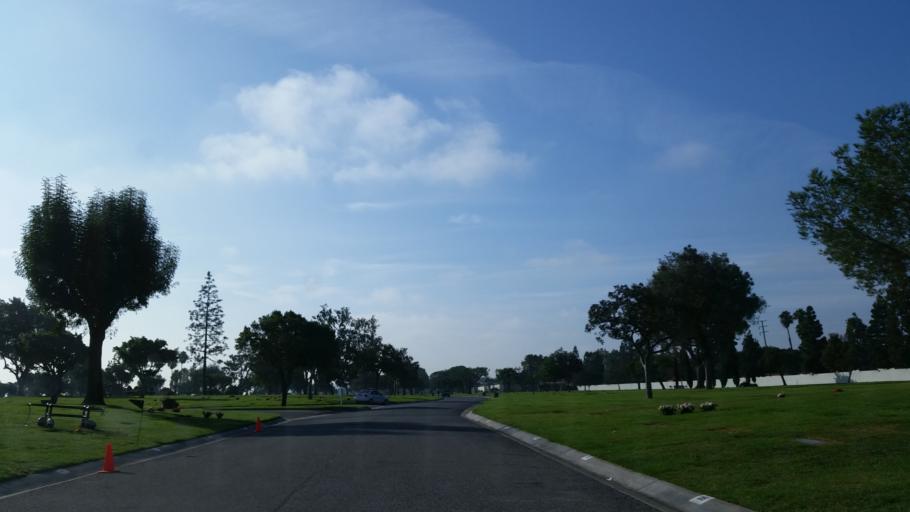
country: US
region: California
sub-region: Los Angeles County
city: Lakewood
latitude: 33.8432
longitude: -118.1664
